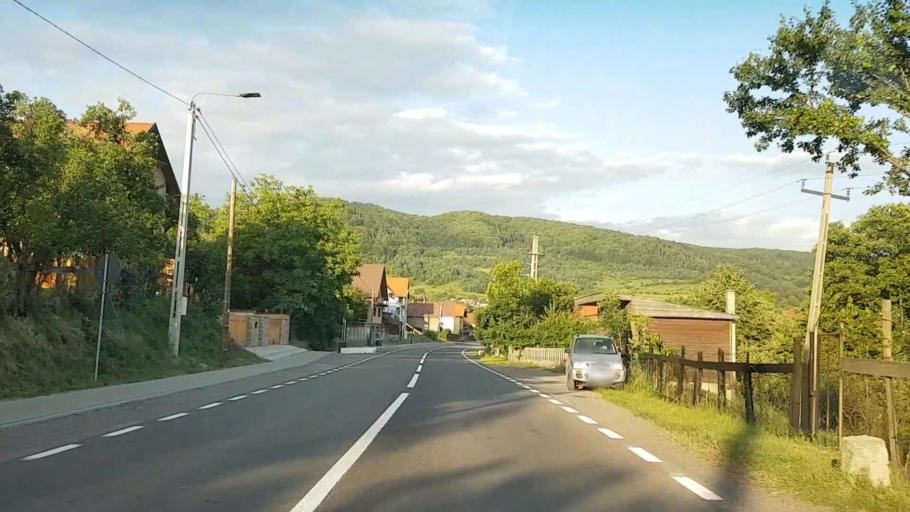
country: RO
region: Harghita
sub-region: Comuna Corund
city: Corund
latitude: 46.4702
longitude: 25.1892
